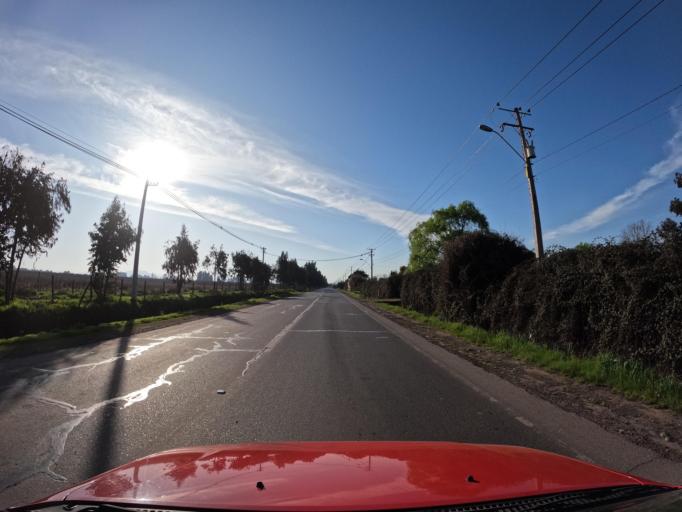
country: CL
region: Maule
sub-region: Provincia de Curico
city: Teno
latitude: -34.8786
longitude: -71.0805
